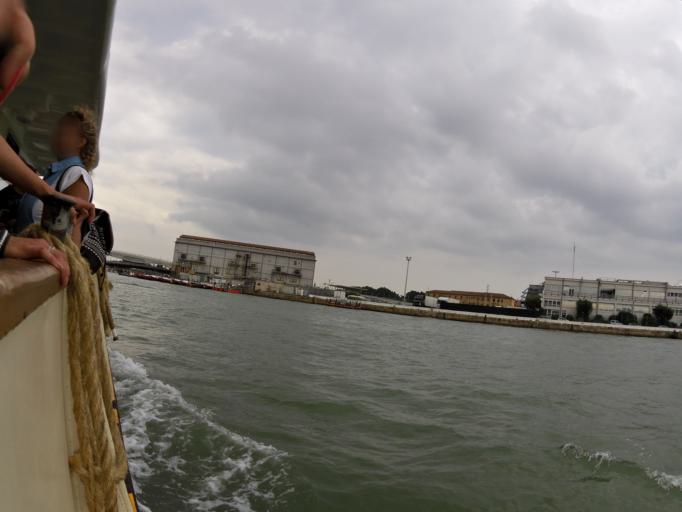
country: IT
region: Veneto
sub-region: Provincia di Venezia
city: Venice
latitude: 45.4403
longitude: 12.3075
